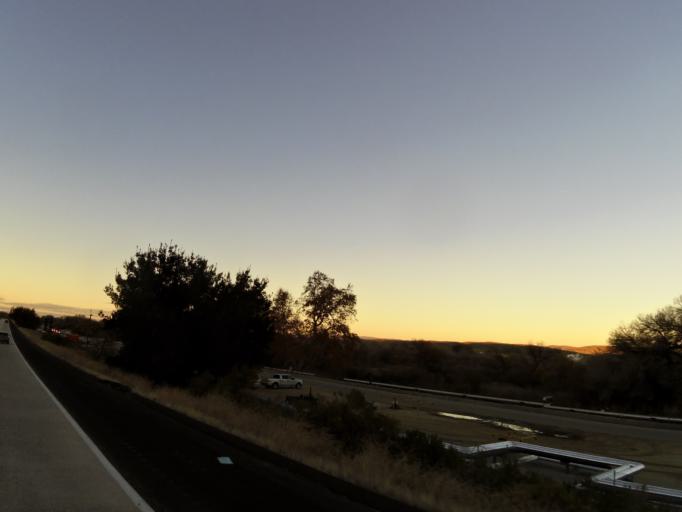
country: US
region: California
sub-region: San Luis Obispo County
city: Lake Nacimiento
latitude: 35.9541
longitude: -120.8803
